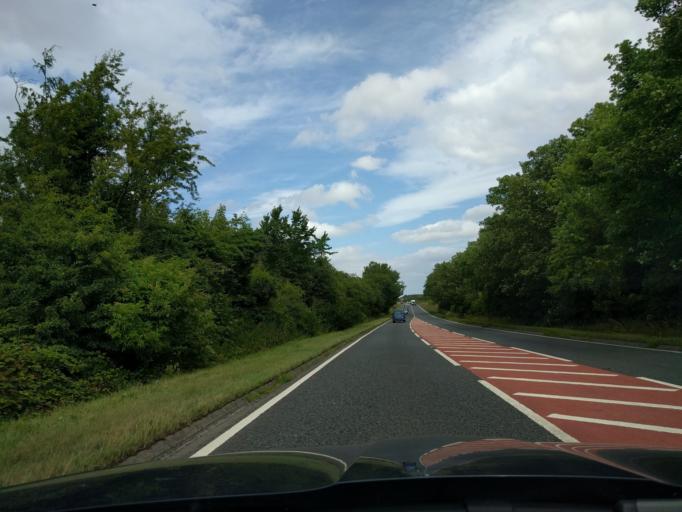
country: GB
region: England
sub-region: Northumberland
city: Felton
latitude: 55.2441
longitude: -1.7035
